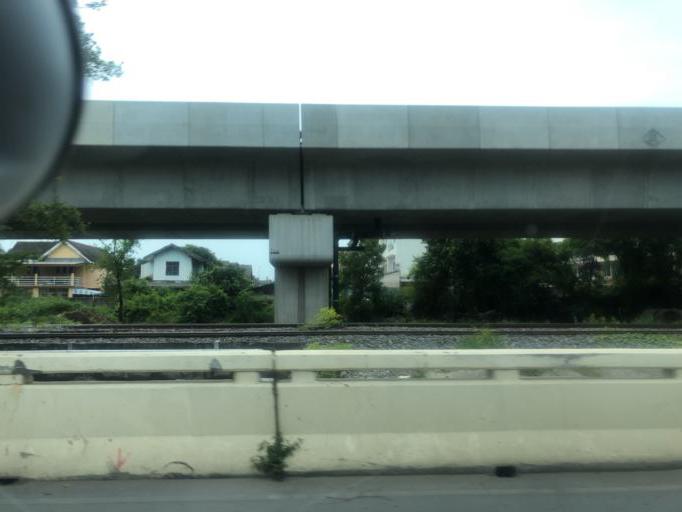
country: TH
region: Bangkok
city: Don Mueang
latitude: 13.9394
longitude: 100.6083
